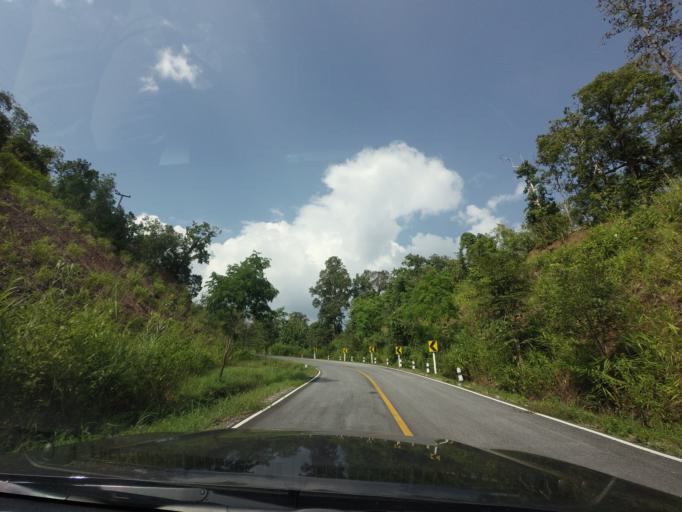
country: TH
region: Uttaradit
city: Ban Khok
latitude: 18.2228
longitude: 101.0349
